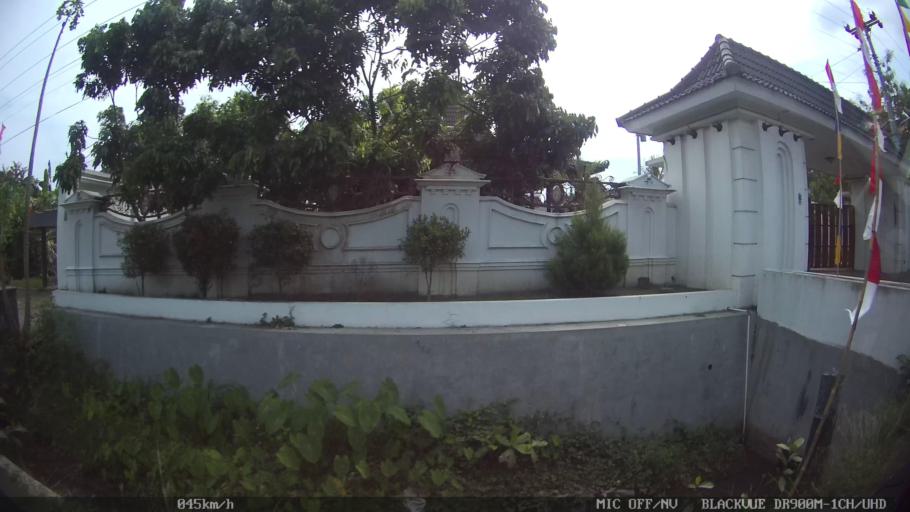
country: ID
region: Central Java
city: Candi Prambanan
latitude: -7.7444
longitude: 110.4812
